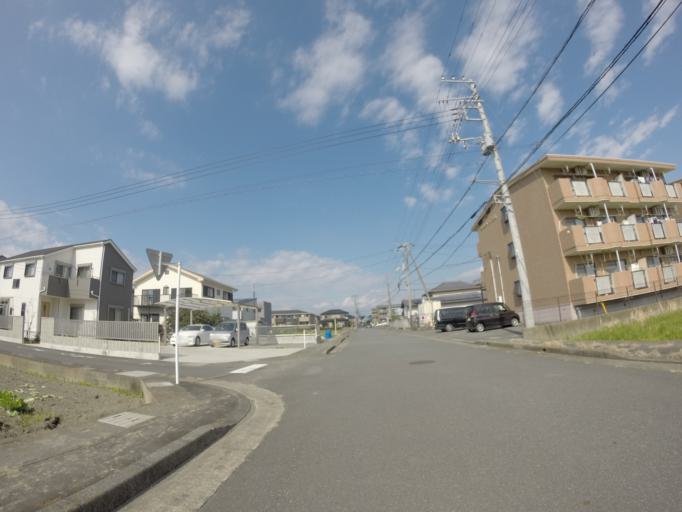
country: JP
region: Shizuoka
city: Fuji
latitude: 35.1324
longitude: 138.6637
